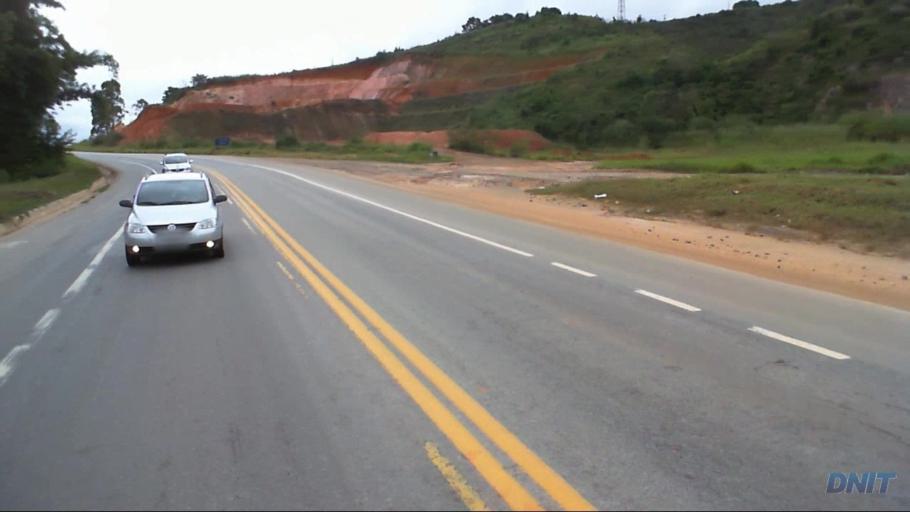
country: BR
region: Minas Gerais
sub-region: Joao Monlevade
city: Joao Monlevade
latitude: -19.8463
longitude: -43.2044
